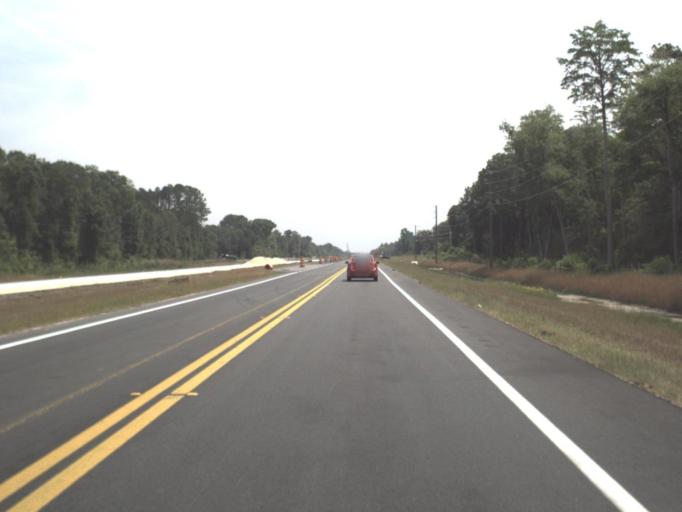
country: US
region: Florida
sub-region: Nassau County
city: Callahan
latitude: 30.5172
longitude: -81.8710
